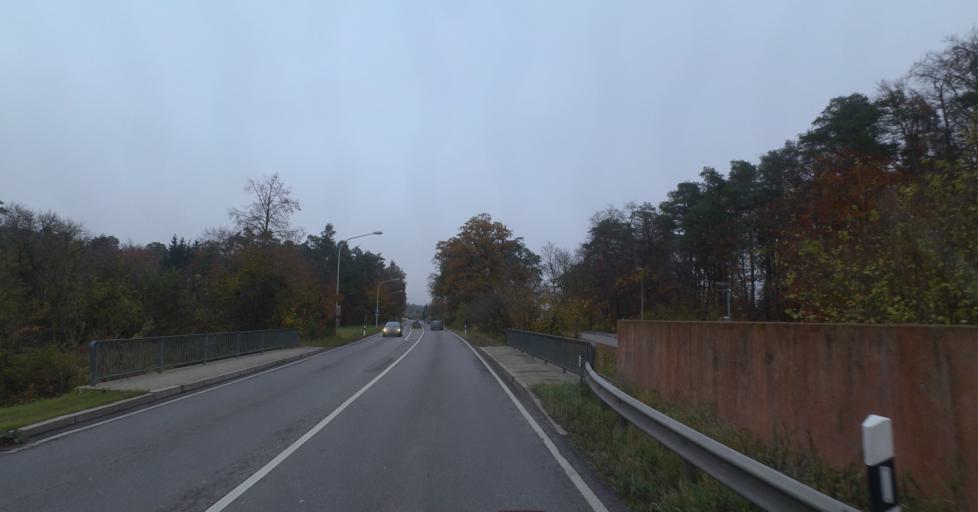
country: DE
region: Bavaria
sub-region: Upper Bavaria
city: Garching an der Alz
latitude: 48.1375
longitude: 12.5957
